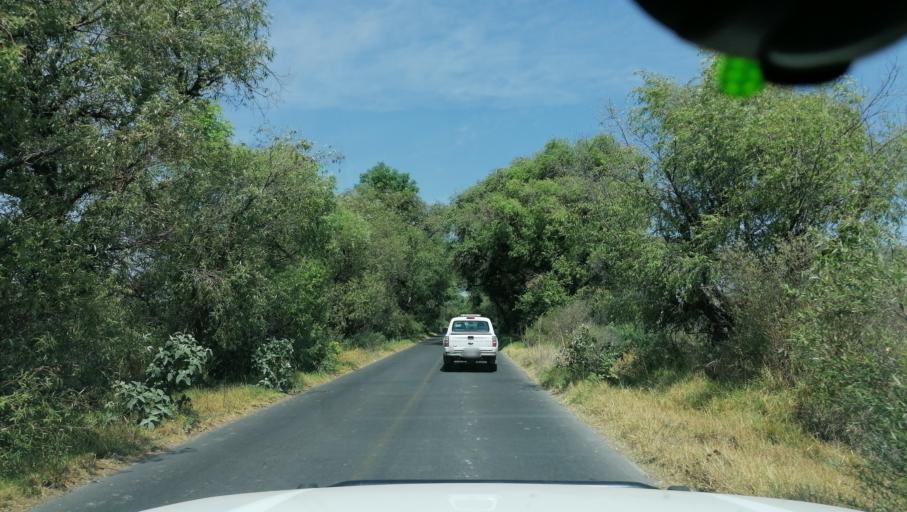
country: MX
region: Tlaxcala
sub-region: Tetlatlahuca
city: Tetlatlahuca
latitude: 19.2044
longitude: -98.2834
